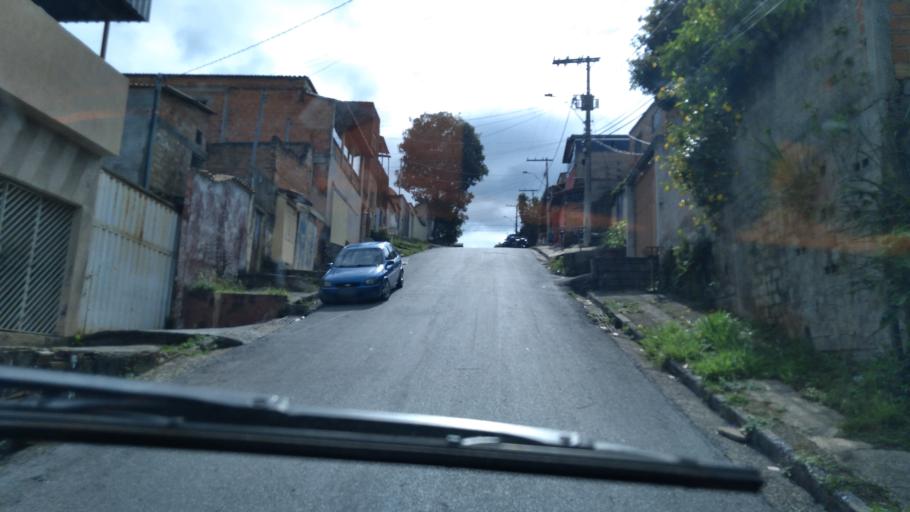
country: BR
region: Minas Gerais
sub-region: Santa Luzia
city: Santa Luzia
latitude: -19.8321
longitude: -43.9004
